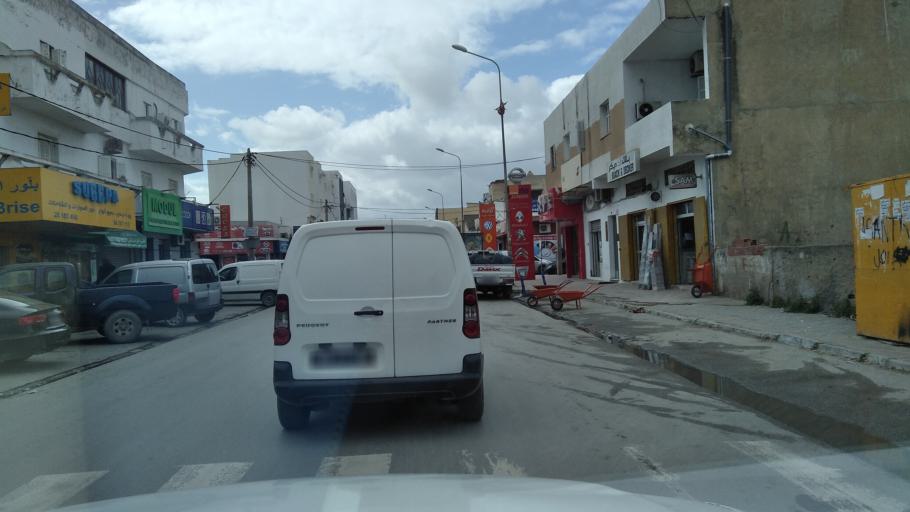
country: TN
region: Bin 'Arus
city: Ben Arous
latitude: 36.7631
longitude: 10.2260
